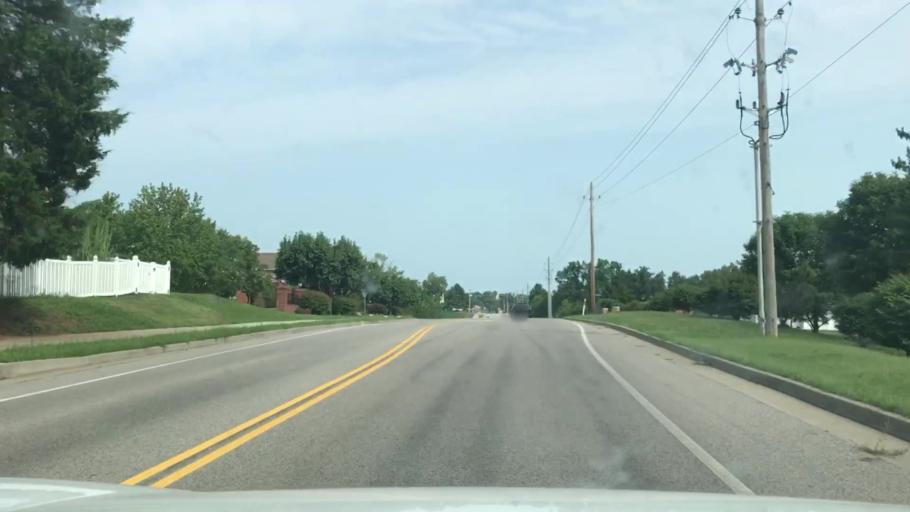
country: US
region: Missouri
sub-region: Saint Charles County
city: Cottleville
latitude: 38.7226
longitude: -90.6428
